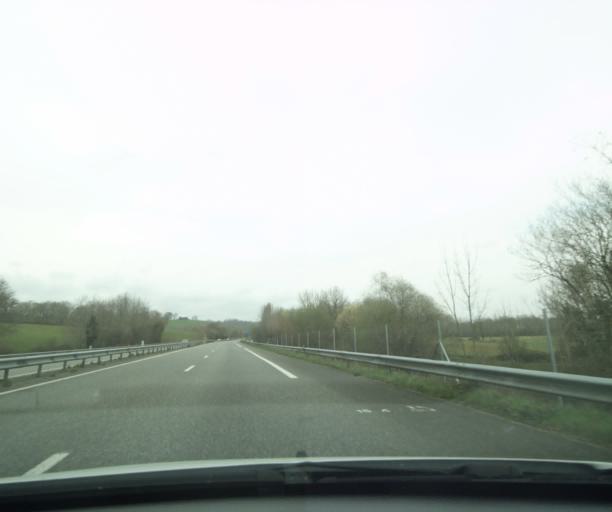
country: FR
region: Aquitaine
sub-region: Departement des Pyrenees-Atlantiques
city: Urt
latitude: 43.4612
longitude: -1.2900
